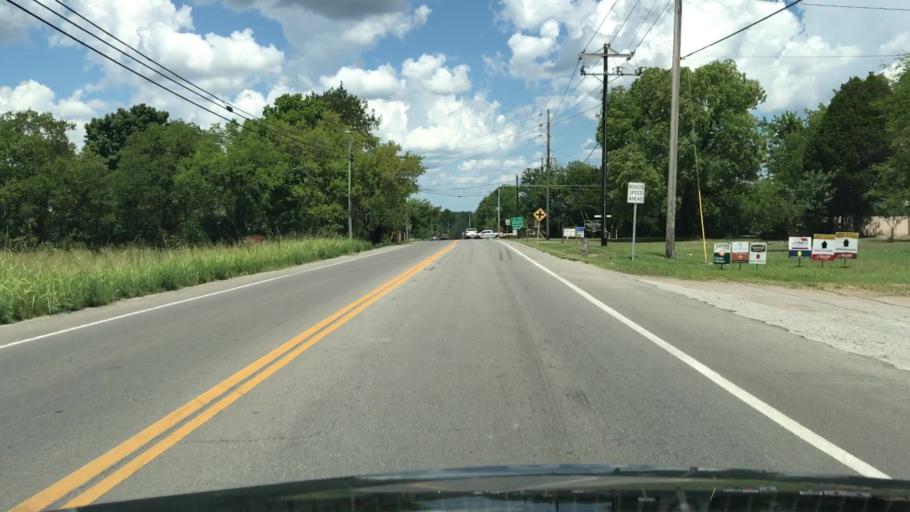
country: US
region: Tennessee
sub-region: Williamson County
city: Nolensville
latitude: 35.9369
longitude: -86.6607
